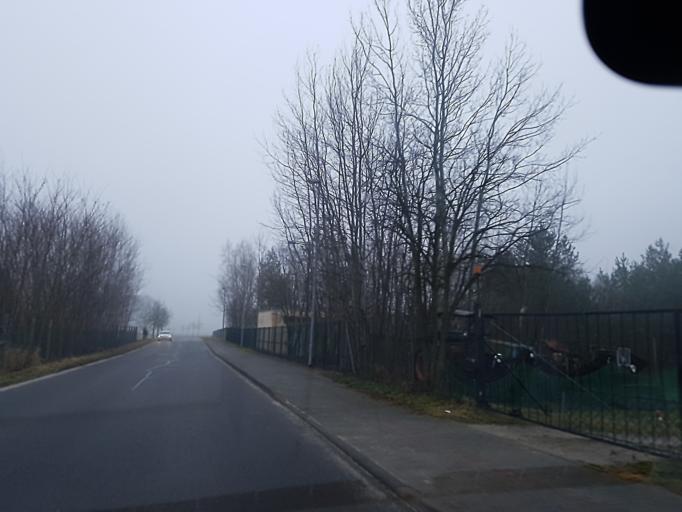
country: DE
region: Brandenburg
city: Finsterwalde
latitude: 51.6329
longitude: 13.7316
